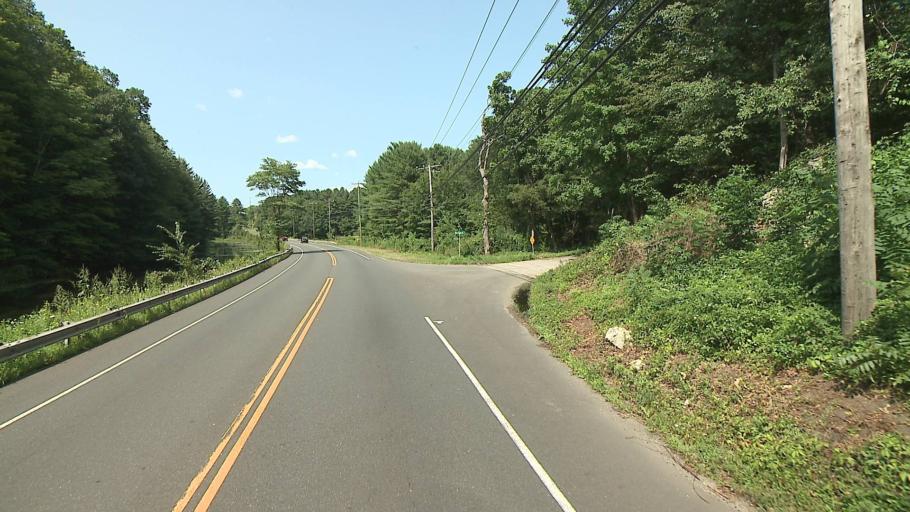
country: US
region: Connecticut
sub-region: Fairfield County
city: Trumbull
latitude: 41.3158
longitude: -73.2603
